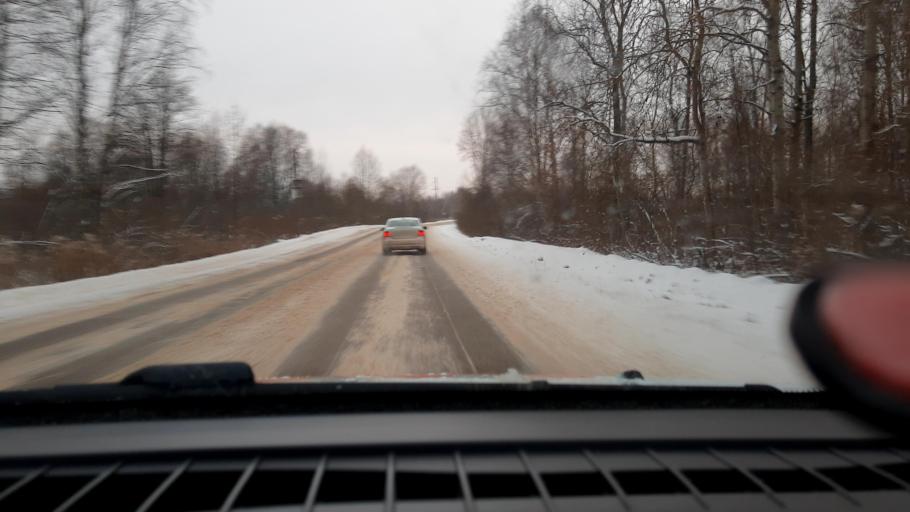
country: RU
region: Nizjnij Novgorod
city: Kstovo
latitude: 56.2796
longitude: 44.3681
